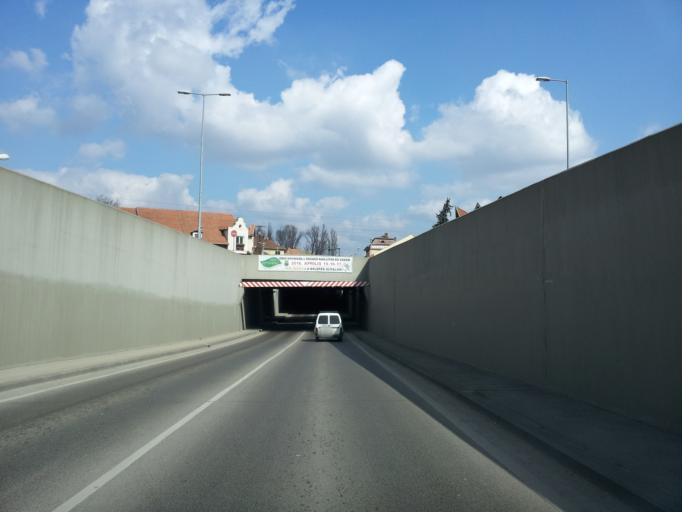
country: HU
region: Pest
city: Erd
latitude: 47.3790
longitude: 18.9222
